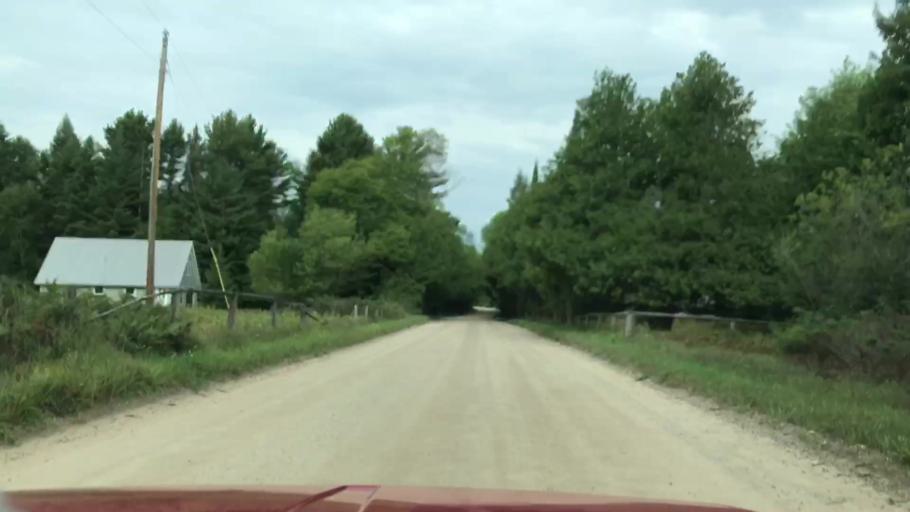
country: US
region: Michigan
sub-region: Charlevoix County
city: Charlevoix
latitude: 45.7282
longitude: -85.5381
